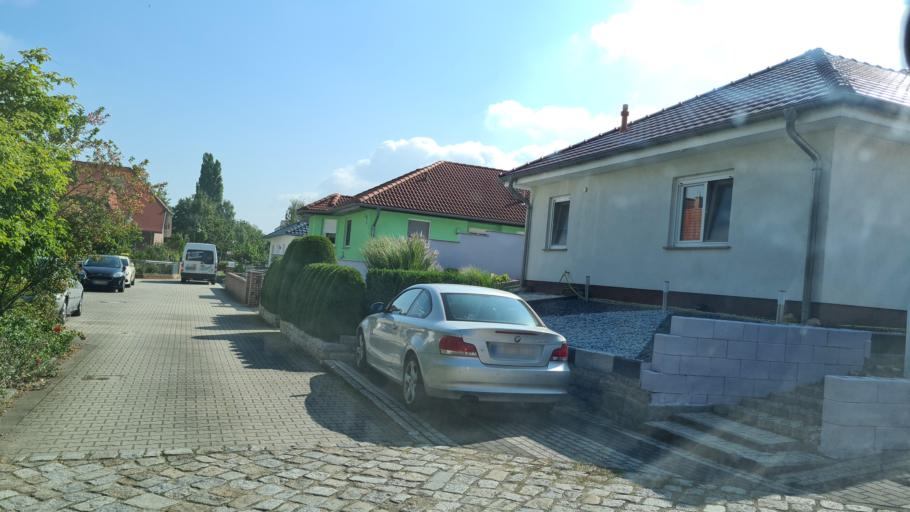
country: DE
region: Brandenburg
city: Luckau
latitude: 51.8561
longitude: 13.6944
